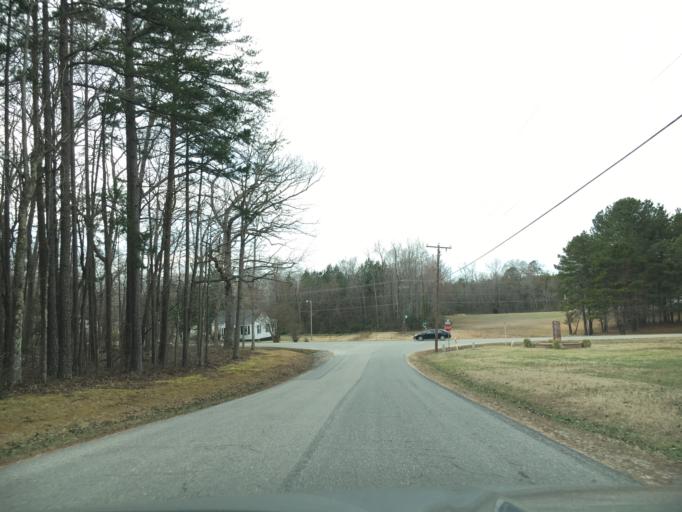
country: US
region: Virginia
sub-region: Halifax County
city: Halifax
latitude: 36.7318
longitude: -78.9367
